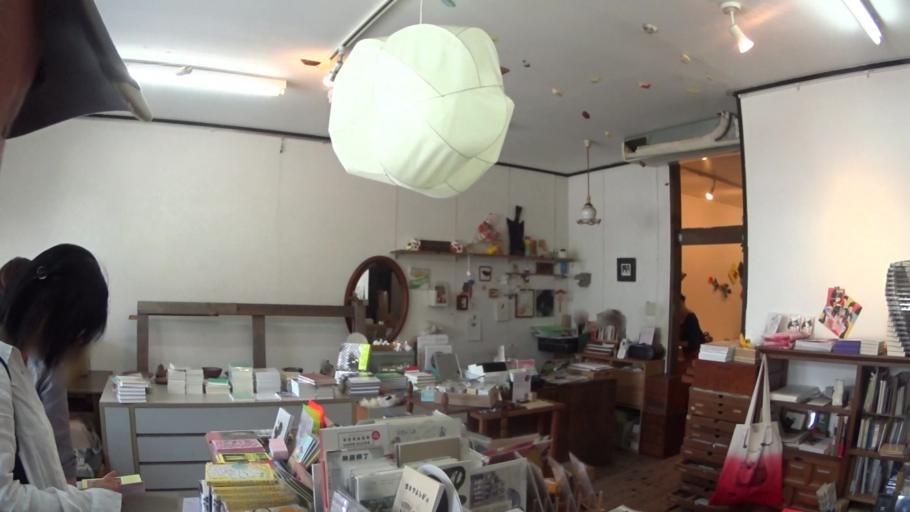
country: JP
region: Tokyo
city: Tokyo
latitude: 35.7256
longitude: 139.7053
